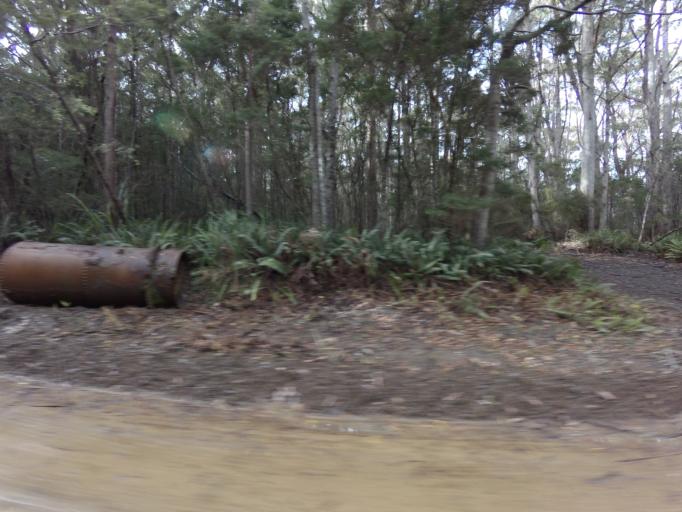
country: AU
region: Tasmania
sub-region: Huon Valley
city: Geeveston
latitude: -43.5647
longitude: 146.8889
